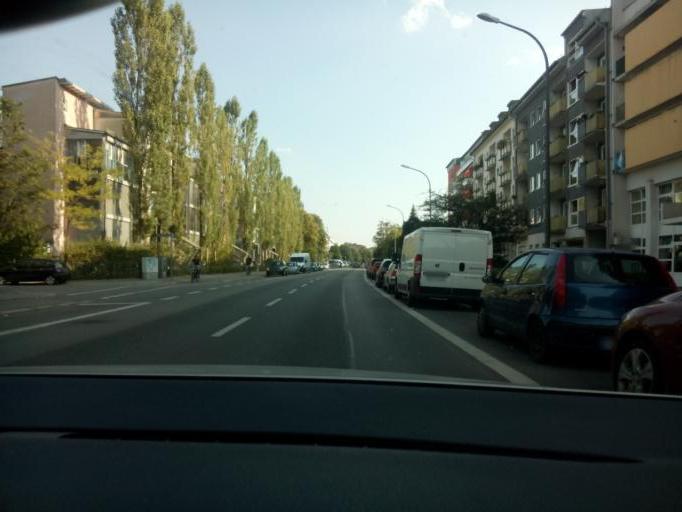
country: DE
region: Bavaria
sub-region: Upper Bavaria
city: Munich
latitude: 48.1131
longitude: 11.6037
